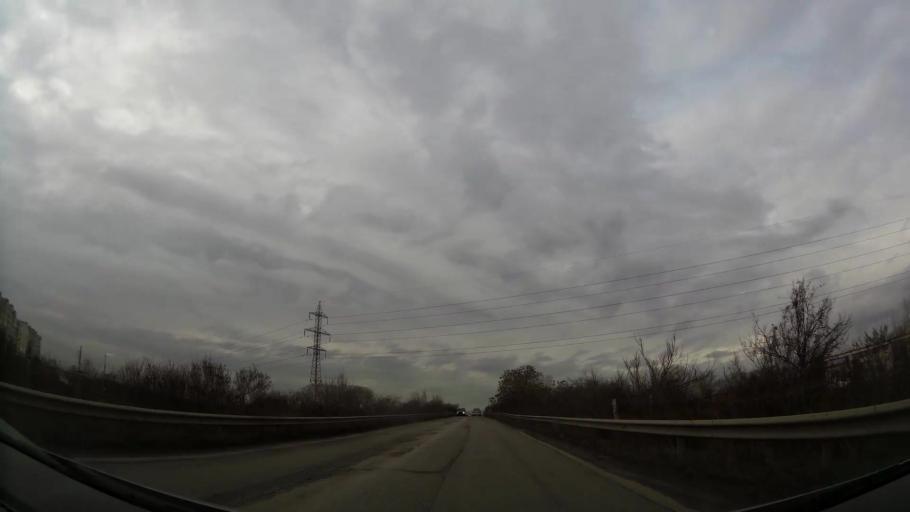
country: BG
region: Sofia-Capital
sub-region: Stolichna Obshtina
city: Sofia
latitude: 42.7487
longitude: 23.2783
